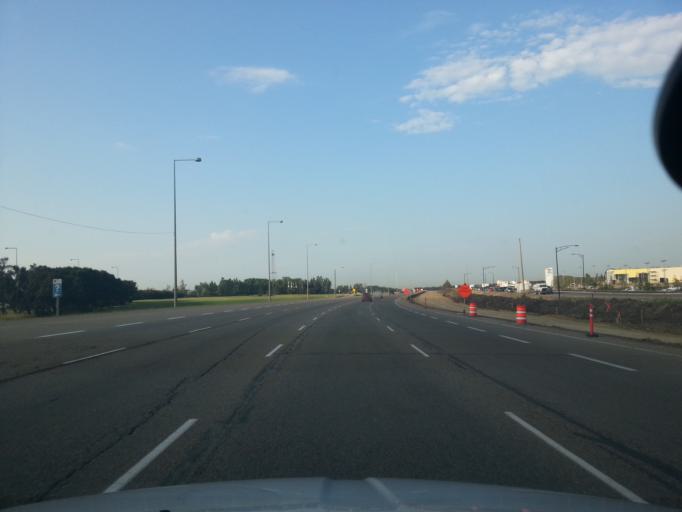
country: CA
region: Alberta
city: Beaumont
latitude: 53.4174
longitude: -113.4947
